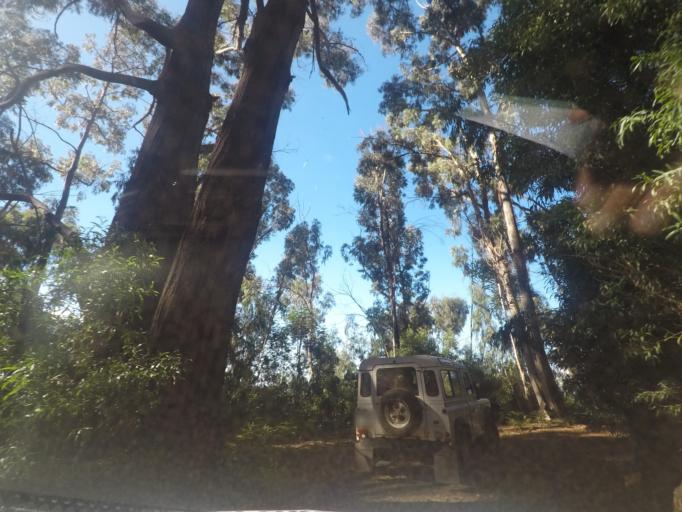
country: PT
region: Madeira
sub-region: Funchal
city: Nossa Senhora do Monte
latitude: 32.6900
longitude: -16.9124
